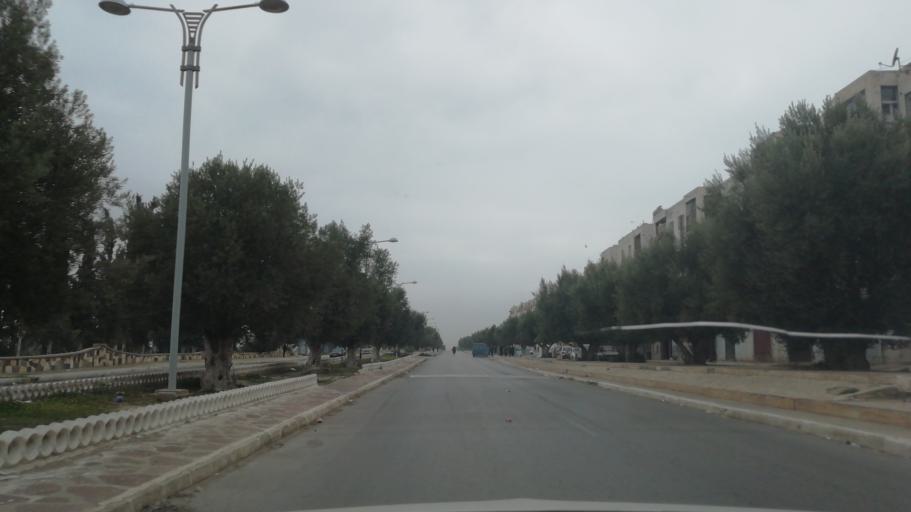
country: DZ
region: Sidi Bel Abbes
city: Sfizef
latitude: 35.2310
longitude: -0.2560
